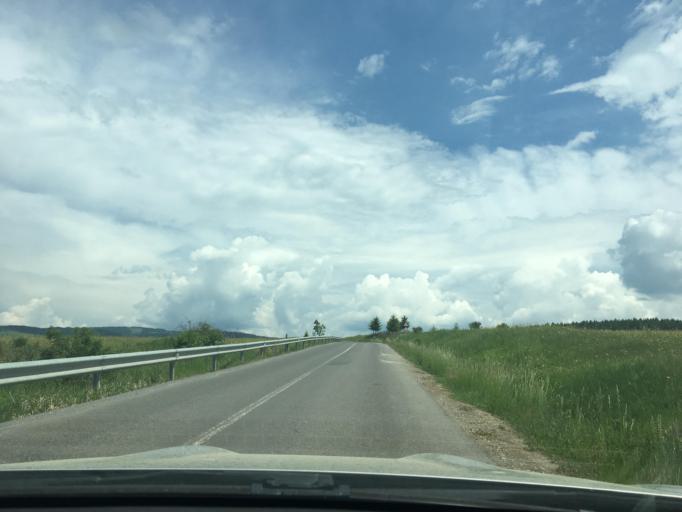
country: RO
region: Harghita
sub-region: Comuna Ditrau
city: Ditrau
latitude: 46.8488
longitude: 25.5029
